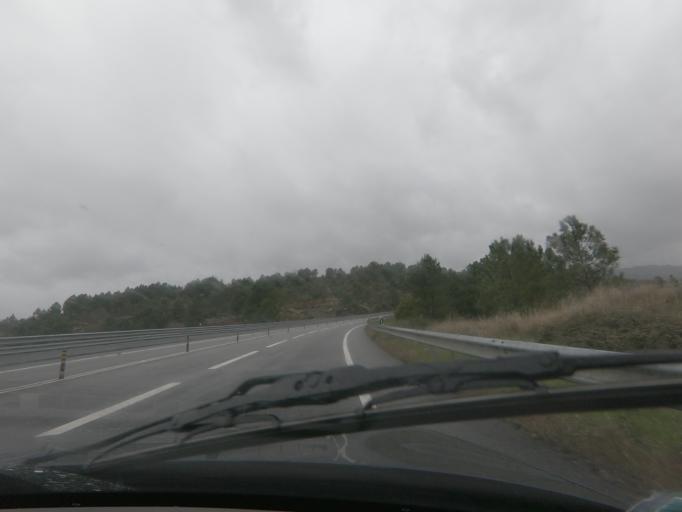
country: PT
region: Vila Real
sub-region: Vila Real
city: Vila Real
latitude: 41.2733
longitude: -7.7912
